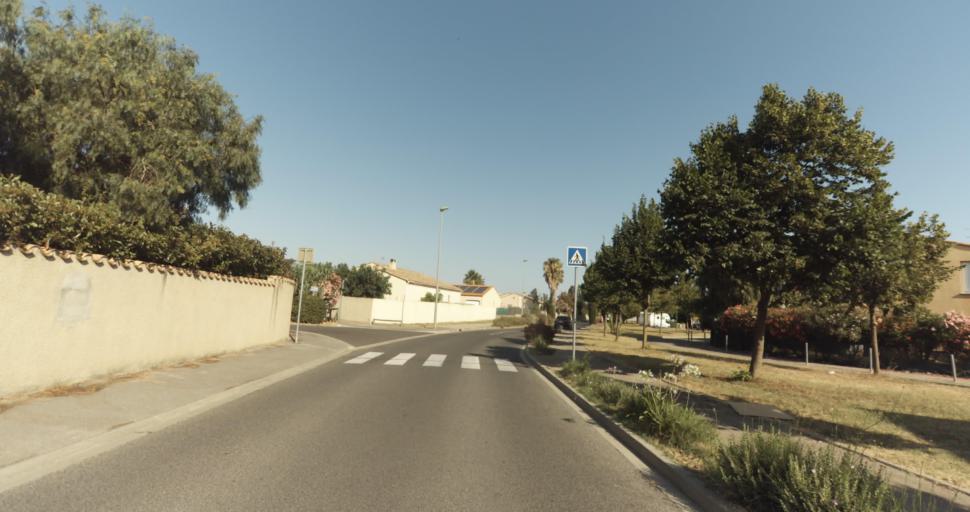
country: FR
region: Languedoc-Roussillon
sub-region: Departement des Pyrenees-Orientales
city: Alenya
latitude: 42.6424
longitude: 2.9775
